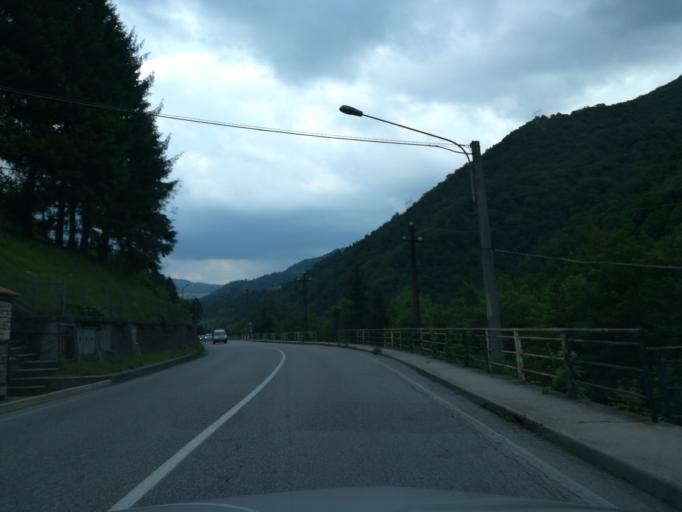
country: IT
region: Lombardy
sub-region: Provincia di Bergamo
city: Strozza
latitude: 45.7749
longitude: 9.5808
